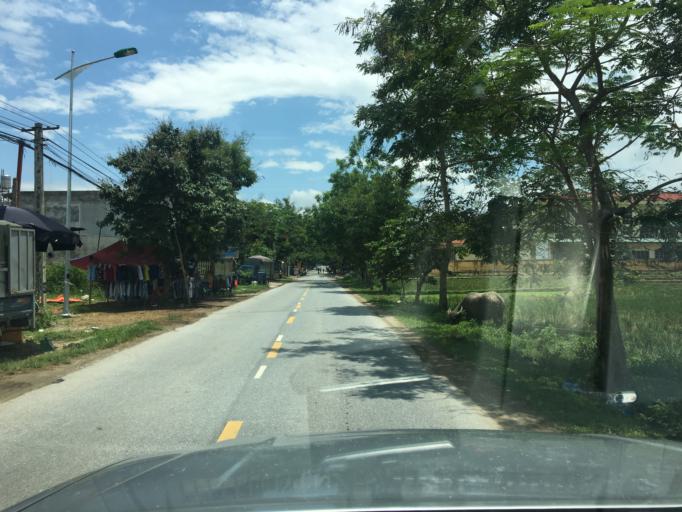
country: VN
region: Yen Bai
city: Son Thinh
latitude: 21.6150
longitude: 104.5074
